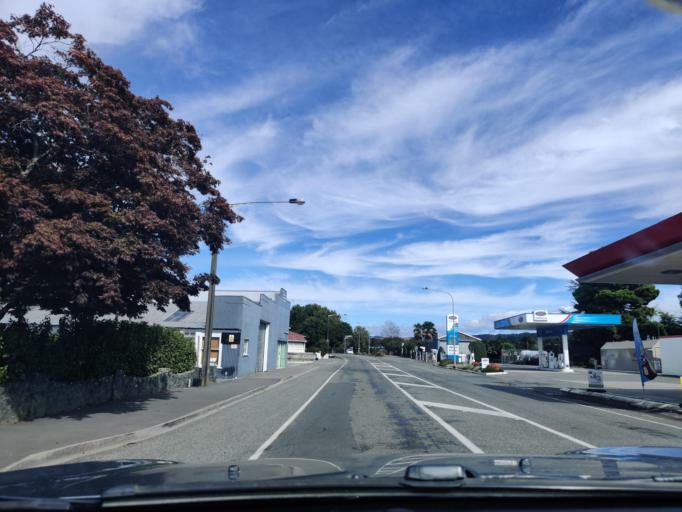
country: NZ
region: Tasman
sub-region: Tasman District
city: Wakefield
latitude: -41.4044
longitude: 173.0457
